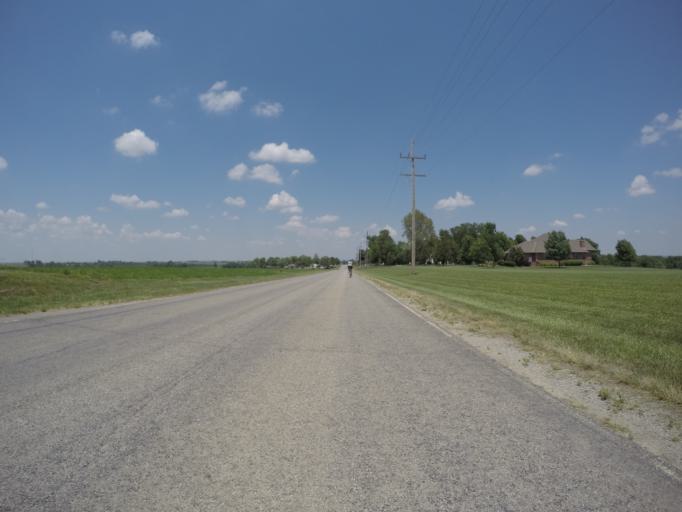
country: US
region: Kansas
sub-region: Doniphan County
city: Troy
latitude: 39.7763
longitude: -95.0969
